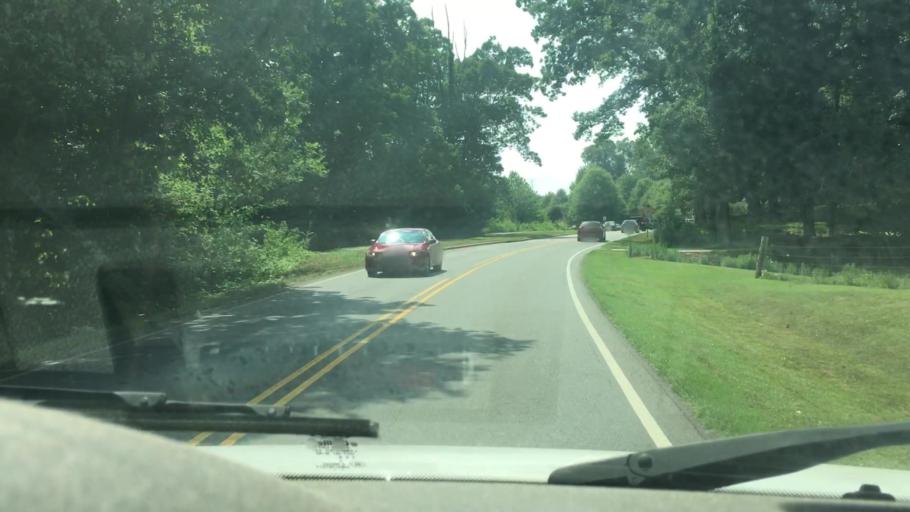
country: US
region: North Carolina
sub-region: Mecklenburg County
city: Huntersville
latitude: 35.4069
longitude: -80.8993
